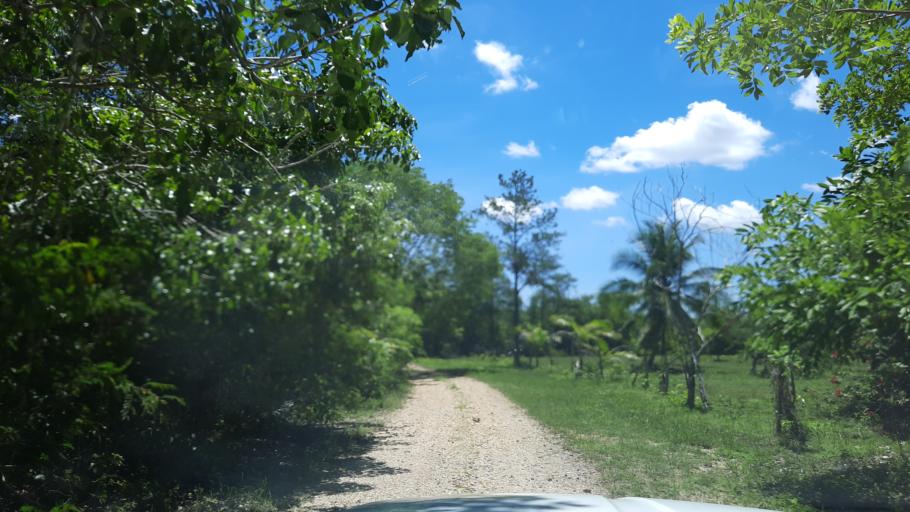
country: BZ
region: Cayo
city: Belmopan
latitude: 17.3562
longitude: -88.5402
